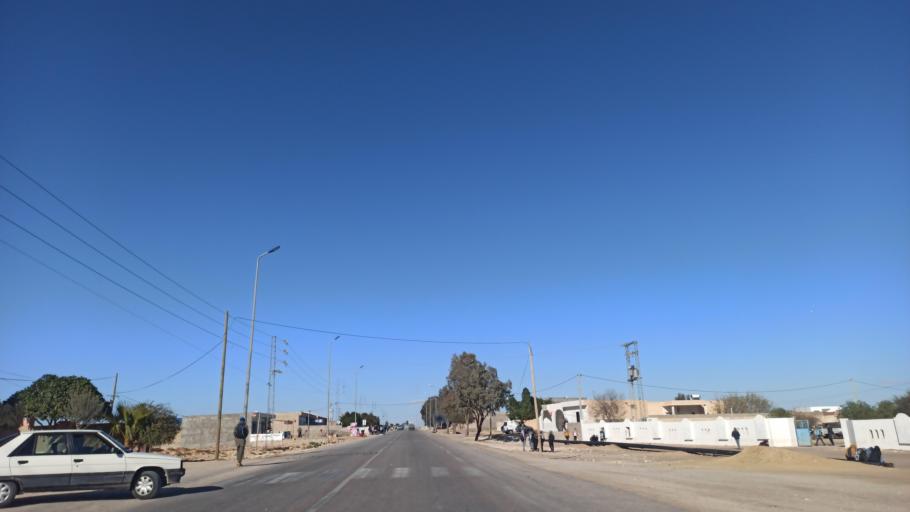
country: TN
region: Sidi Bu Zayd
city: Jilma
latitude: 35.2835
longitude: 9.4189
